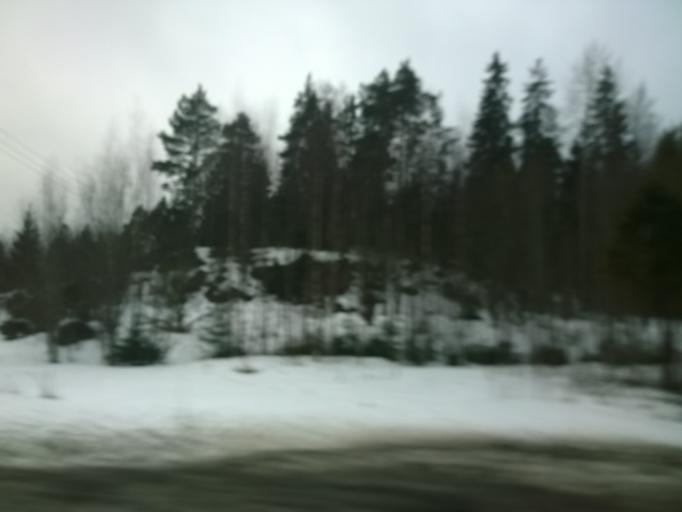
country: FI
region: Pirkanmaa
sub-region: Tampere
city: Lempaeaelae
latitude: 61.3757
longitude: 23.7857
